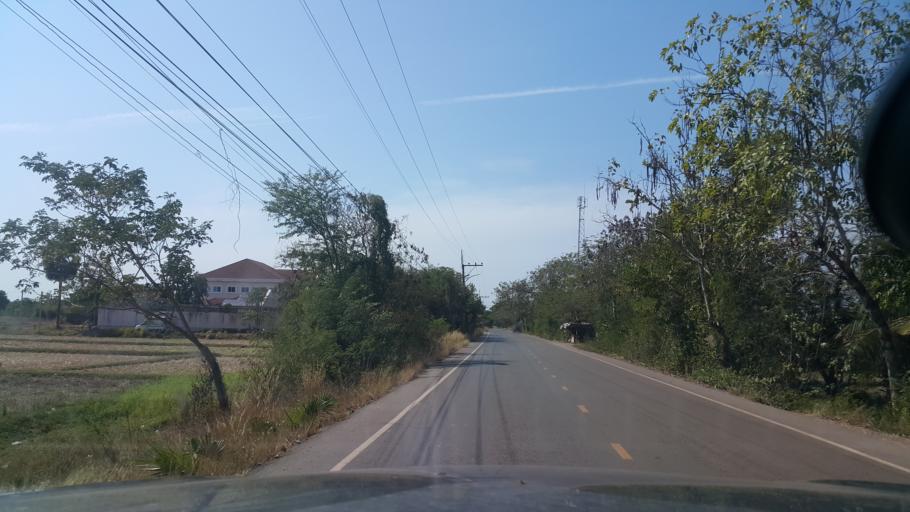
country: TH
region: Changwat Udon Thani
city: Udon Thani
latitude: 17.5065
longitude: 102.7546
